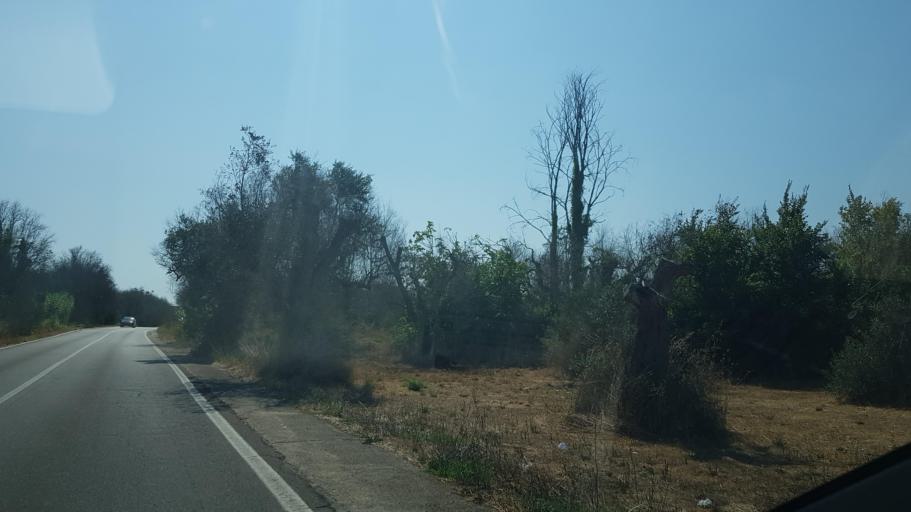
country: IT
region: Apulia
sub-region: Provincia di Lecce
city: Montesano Salentino
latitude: 40.0039
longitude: 18.2965
